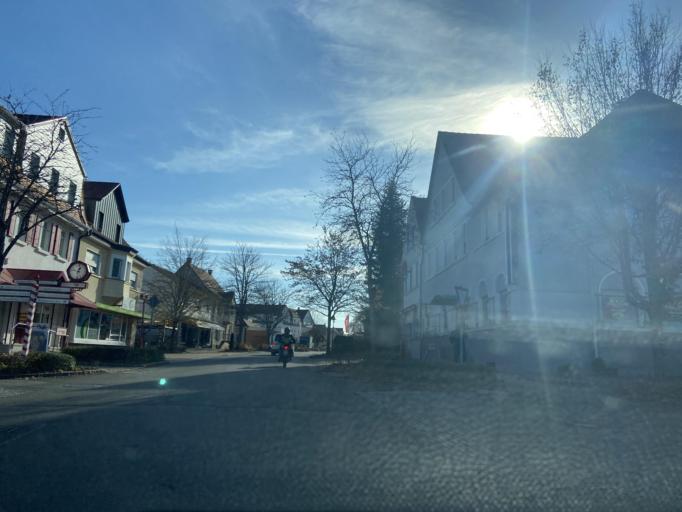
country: DE
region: Baden-Wuerttemberg
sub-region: Tuebingen Region
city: Stetten am Kalten Markt
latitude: 48.1256
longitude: 9.0773
